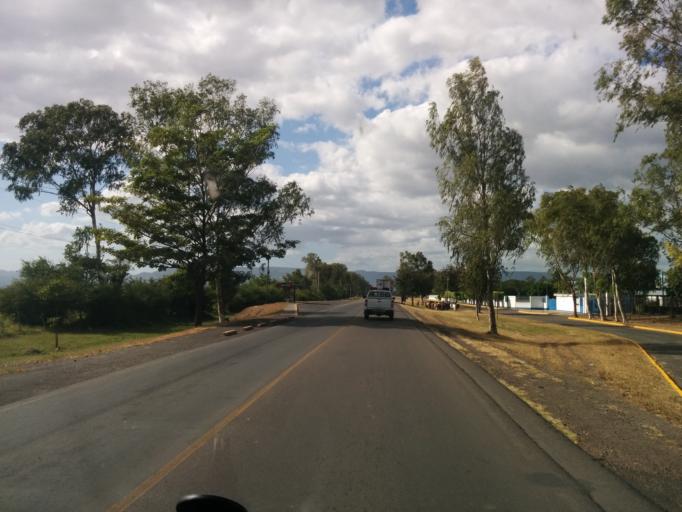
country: NI
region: Matagalpa
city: Ciudad Dario
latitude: 12.8619
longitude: -86.1094
